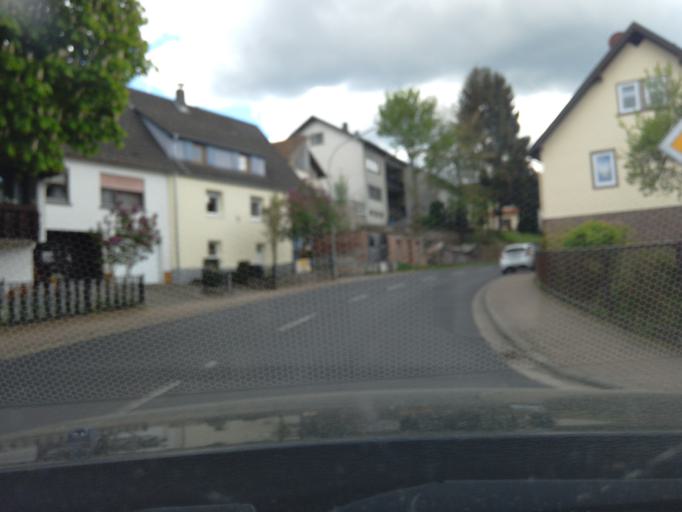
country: DE
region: Bavaria
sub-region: Regierungsbezirk Unterfranken
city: Aura im Sinngrund
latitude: 50.1899
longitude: 9.4727
